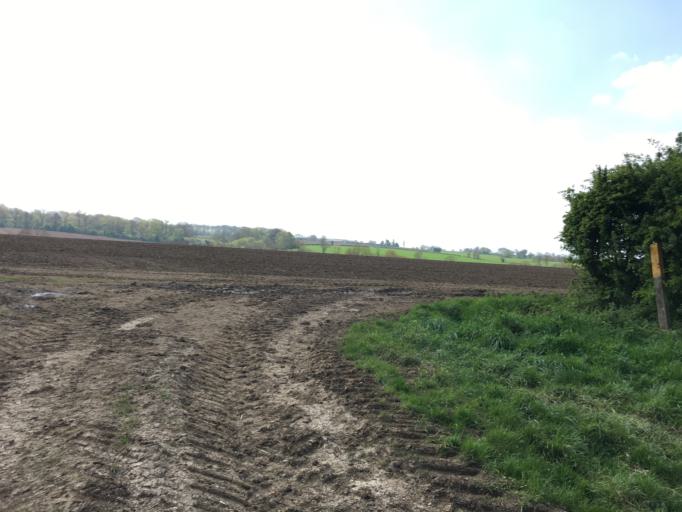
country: GB
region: England
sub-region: Leicestershire
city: Houghton on the Hill
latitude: 52.6095
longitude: -0.9947
